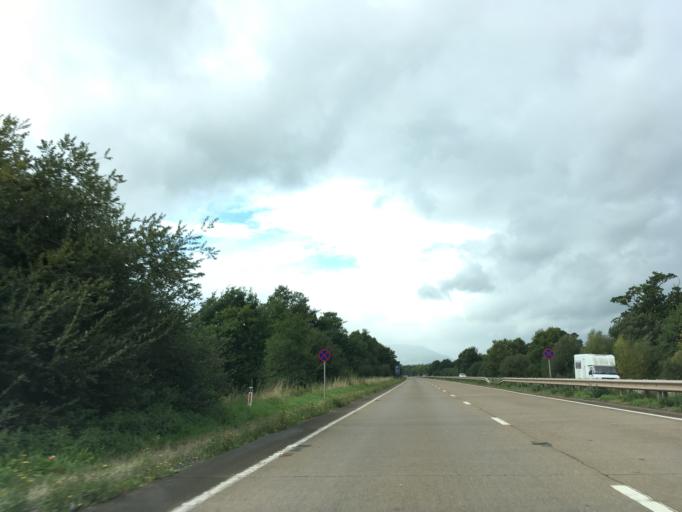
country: GB
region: Wales
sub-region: Monmouthshire
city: Llanarth
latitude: 51.7784
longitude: -2.8958
